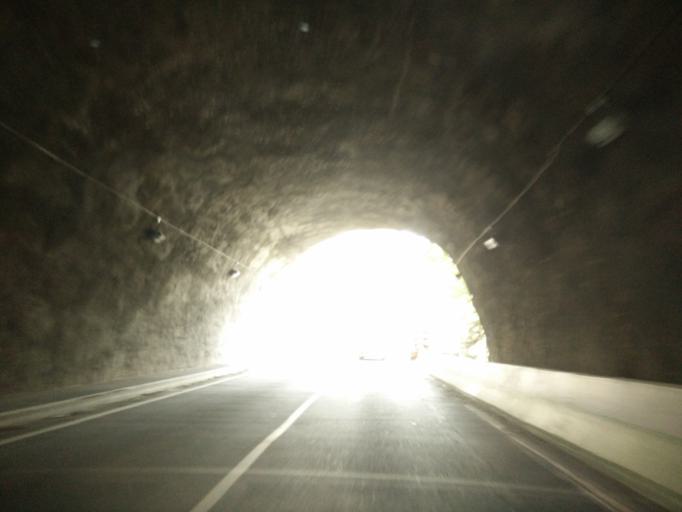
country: MQ
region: Martinique
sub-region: Martinique
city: Saint-Pierre
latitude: 14.7310
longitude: -61.1798
